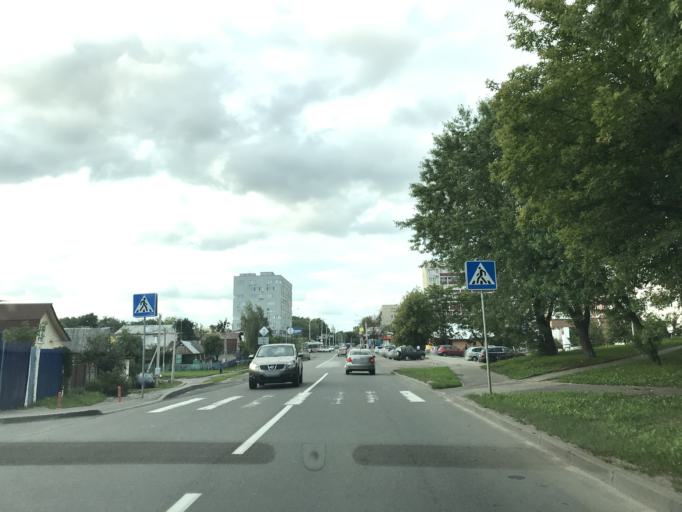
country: BY
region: Minsk
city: Minsk
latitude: 53.9506
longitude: 27.6014
